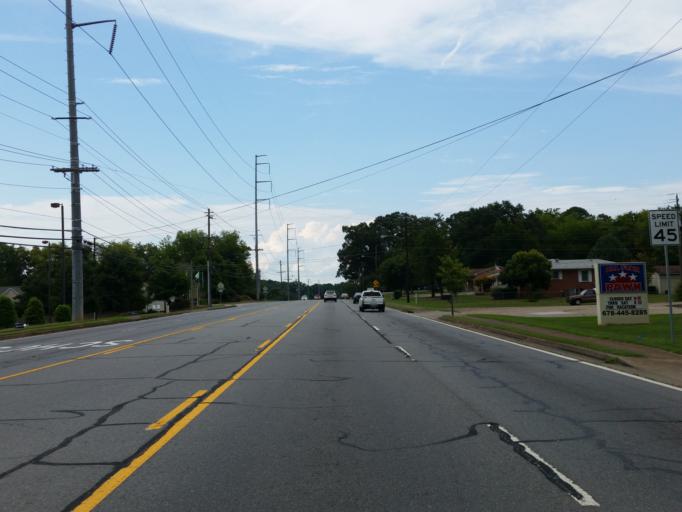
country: US
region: Georgia
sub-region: Cherokee County
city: Woodstock
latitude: 34.0391
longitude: -84.5284
